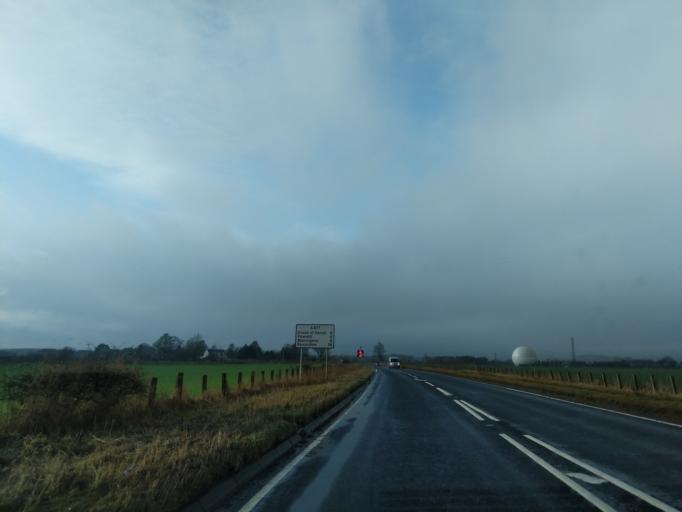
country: GB
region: Scotland
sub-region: Perth and Kinross
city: Kinross
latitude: 56.2091
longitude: -3.4533
